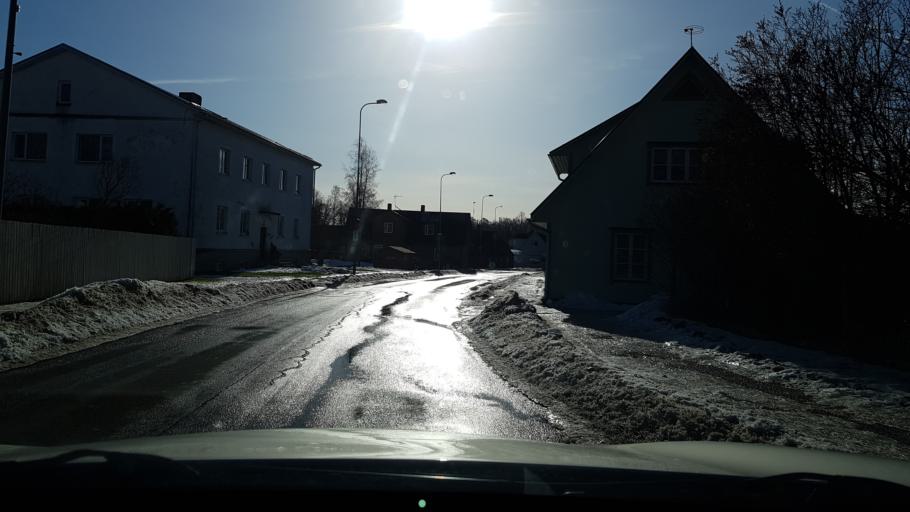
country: EE
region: Viljandimaa
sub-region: Suure-Jaani vald
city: Suure-Jaani
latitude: 58.5375
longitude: 25.4697
